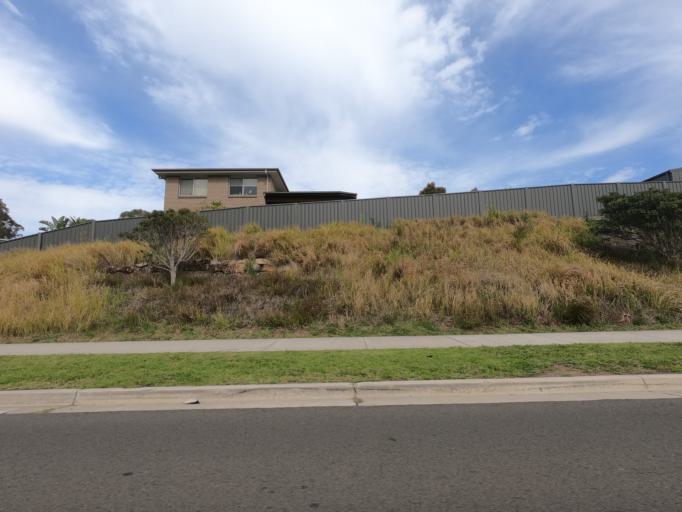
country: AU
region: New South Wales
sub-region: Wollongong
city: Dapto
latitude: -34.4921
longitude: 150.7627
